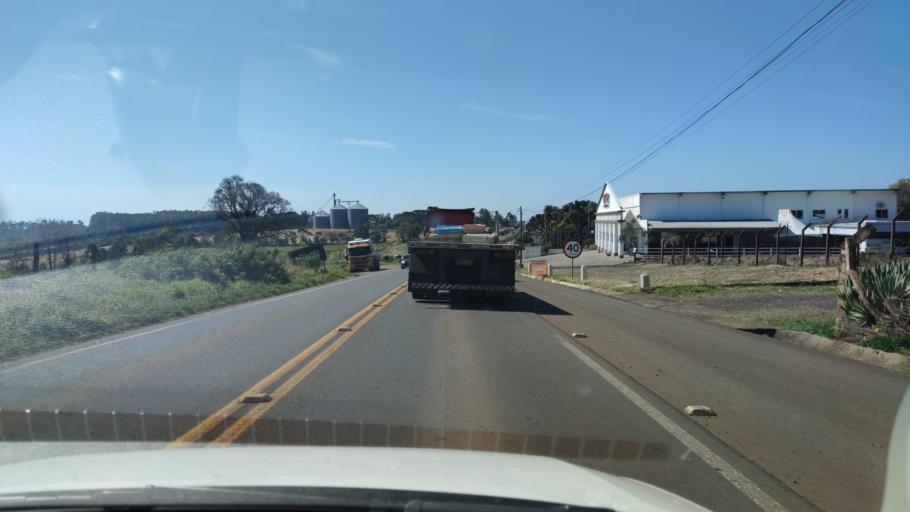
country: BR
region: Santa Catarina
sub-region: Sao Lourenco Do Oeste
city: Sao Lourenco dOeste
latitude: -26.3490
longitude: -52.8552
